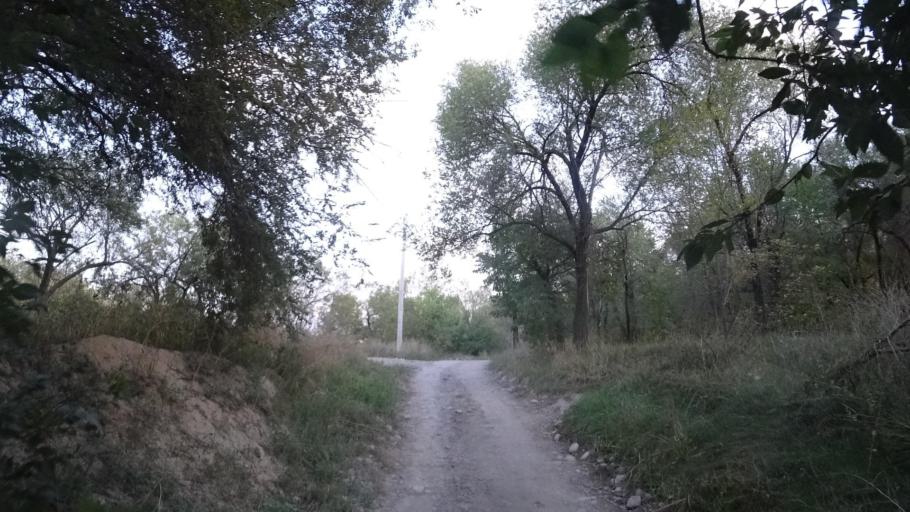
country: KZ
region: Almaty Oblysy
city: Pervomayskiy
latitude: 43.3371
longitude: 76.9978
